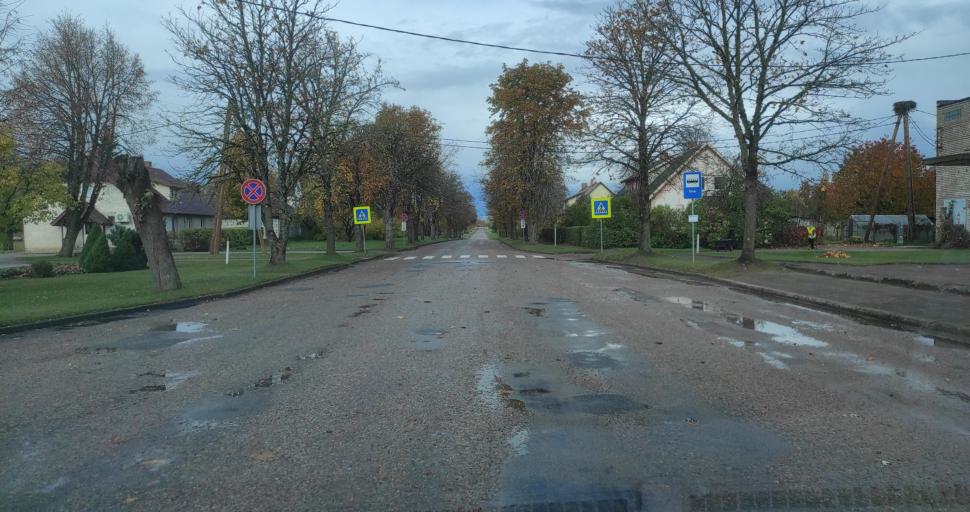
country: LV
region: Vainode
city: Vainode
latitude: 56.5693
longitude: 21.9002
